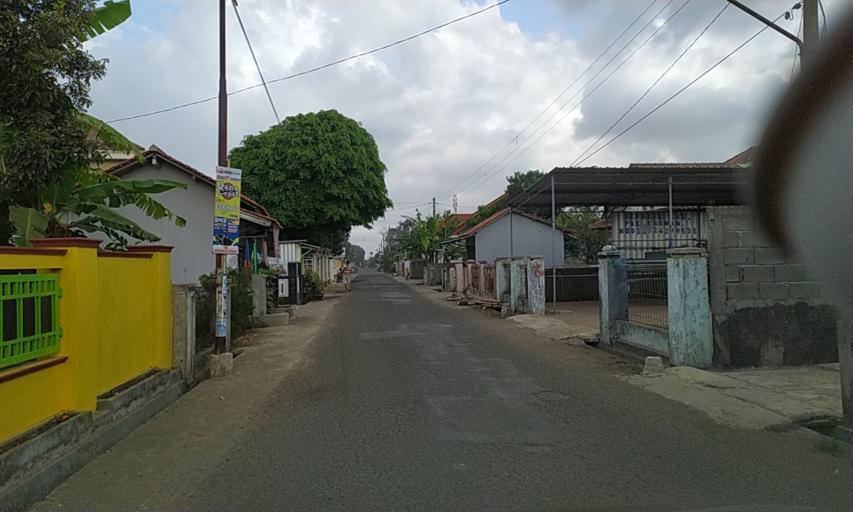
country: ID
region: Central Java
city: Rejanegara
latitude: -7.6623
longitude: 109.0458
